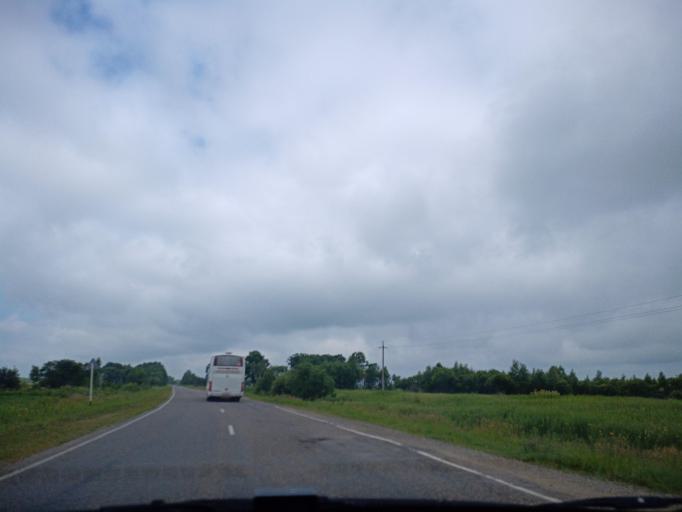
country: RU
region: Primorskiy
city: Novopokrovka
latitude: 45.9745
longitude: 134.2111
